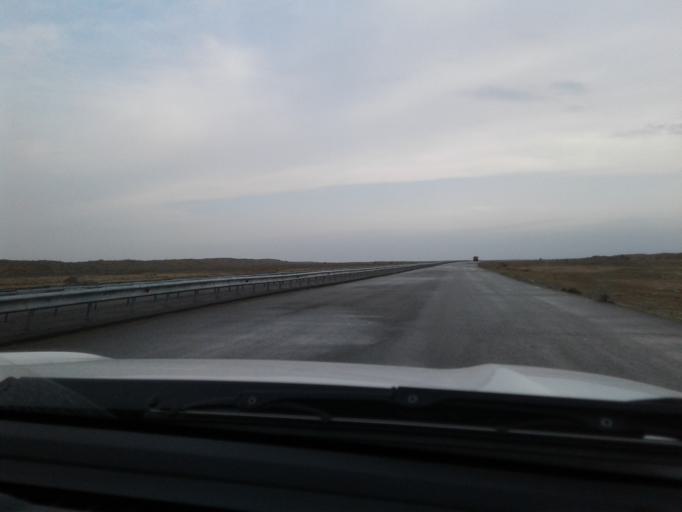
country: TM
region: Ahal
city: Abadan
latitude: 38.4745
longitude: 58.5059
